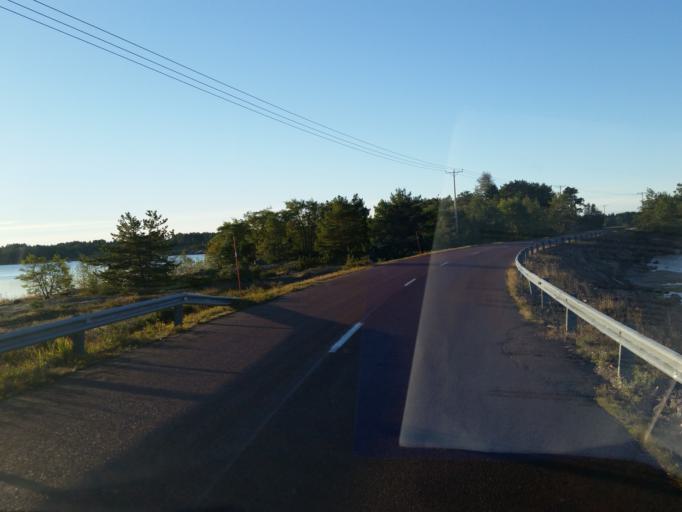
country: AX
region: Alands skaergard
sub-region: Vardoe
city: Vardoe
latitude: 60.3155
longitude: 20.3756
